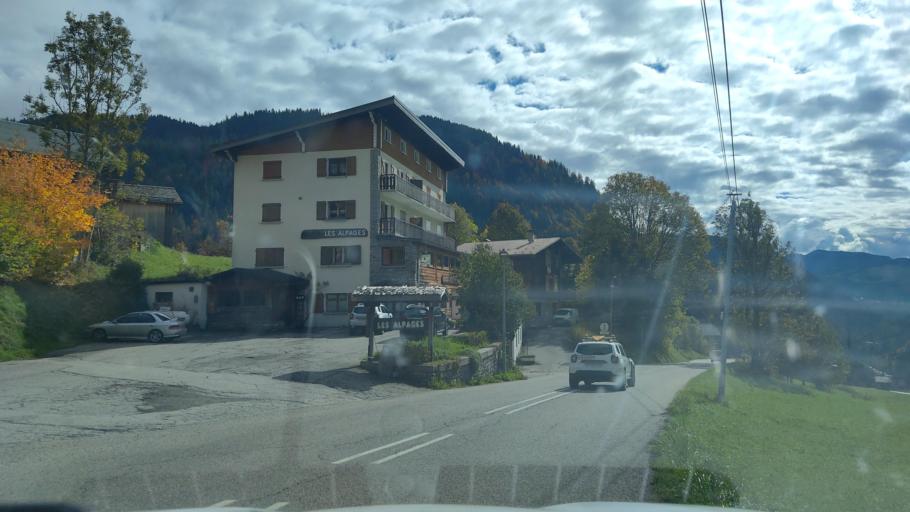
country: FR
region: Rhone-Alpes
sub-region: Departement de la Haute-Savoie
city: La Clusaz
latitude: 45.8667
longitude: 6.4929
